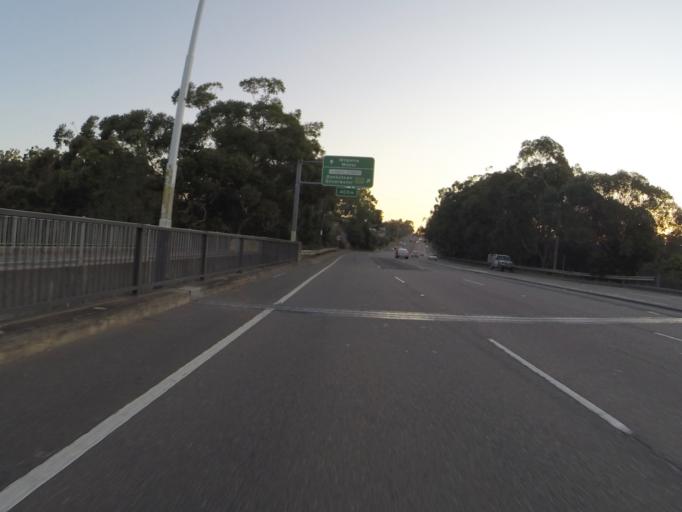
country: AU
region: New South Wales
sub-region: Hurstville
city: Peakhurst
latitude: -33.9635
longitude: 151.0415
